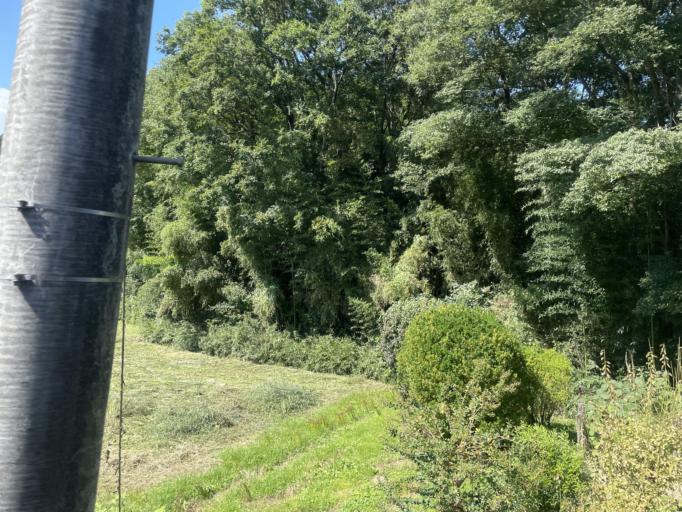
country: JP
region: Nara
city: Gose
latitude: 34.4160
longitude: 135.7483
